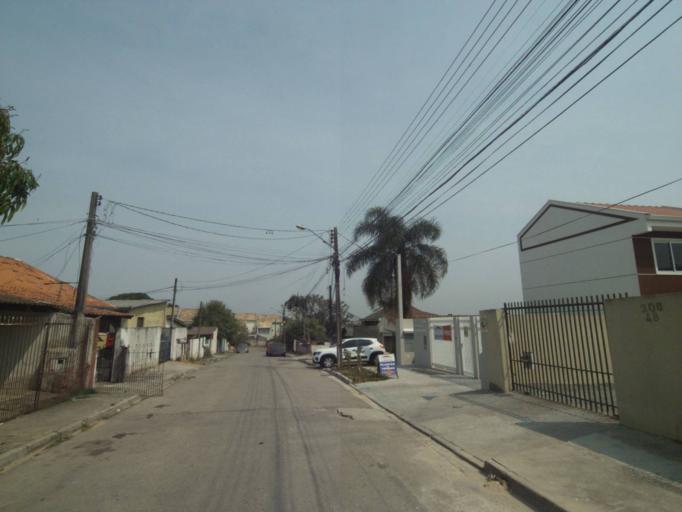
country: BR
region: Parana
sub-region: Pinhais
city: Pinhais
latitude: -25.4834
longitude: -49.2157
